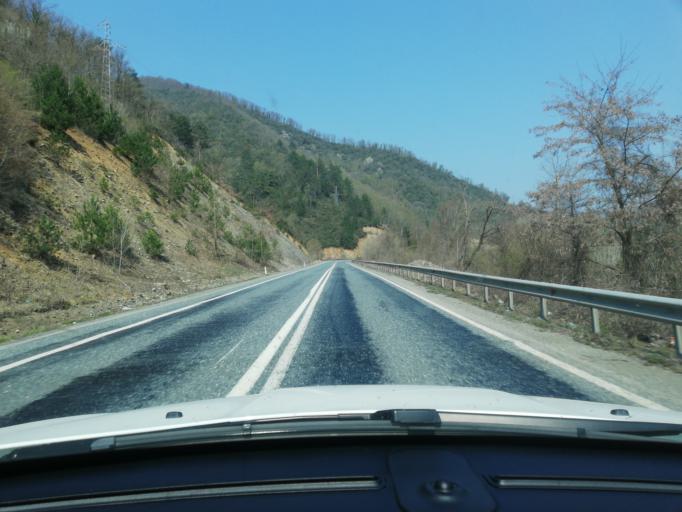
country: TR
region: Zonguldak
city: Gokcebey
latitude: 41.2468
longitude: 32.1684
